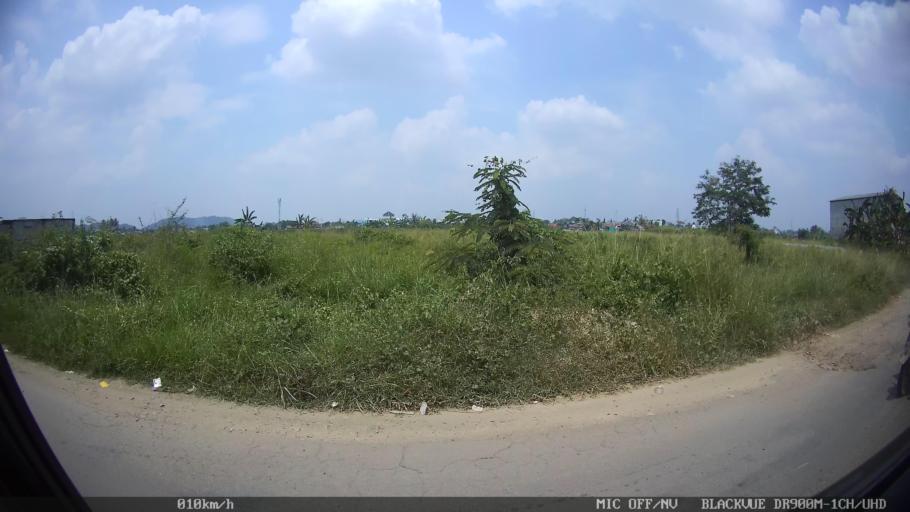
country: ID
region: Lampung
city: Pringsewu
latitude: -5.3550
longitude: 104.9942
